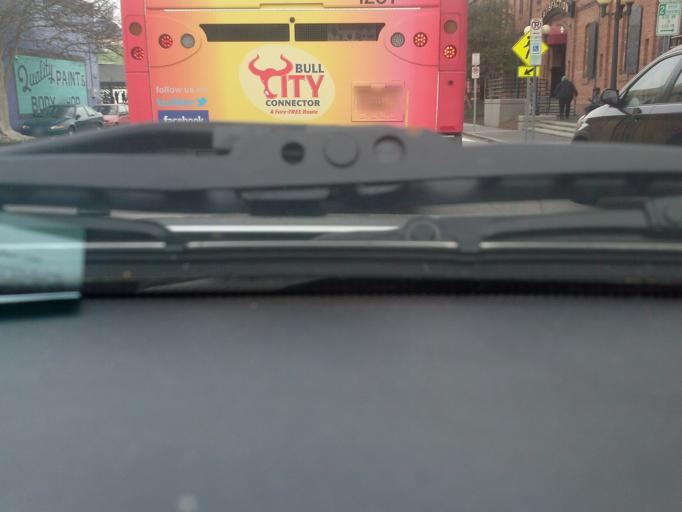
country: US
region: North Carolina
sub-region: Durham County
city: Durham
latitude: 36.0005
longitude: -78.9099
